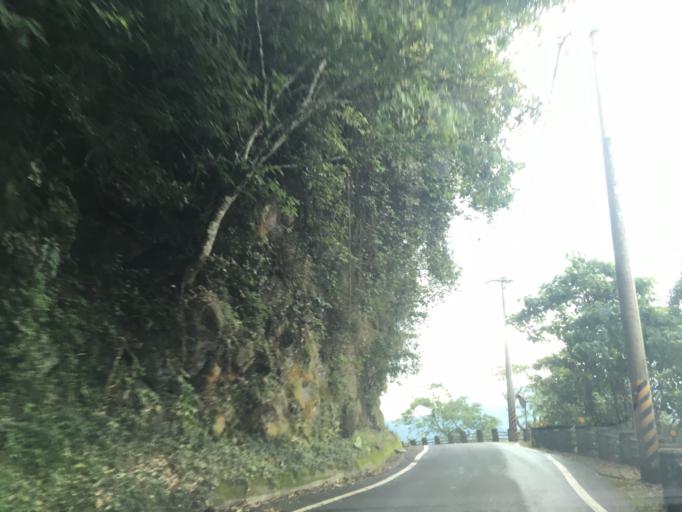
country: TW
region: Taiwan
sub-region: Chiayi
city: Jiayi Shi
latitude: 23.4442
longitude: 120.6620
